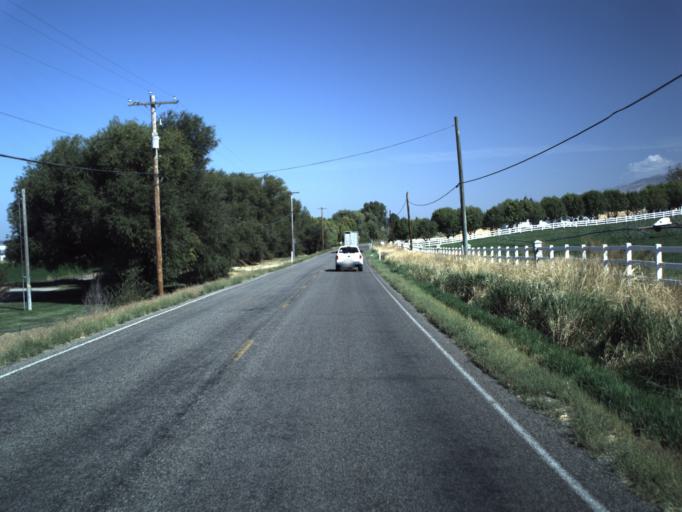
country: US
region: Utah
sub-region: Cache County
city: Hyrum
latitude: 41.5800
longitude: -111.8387
